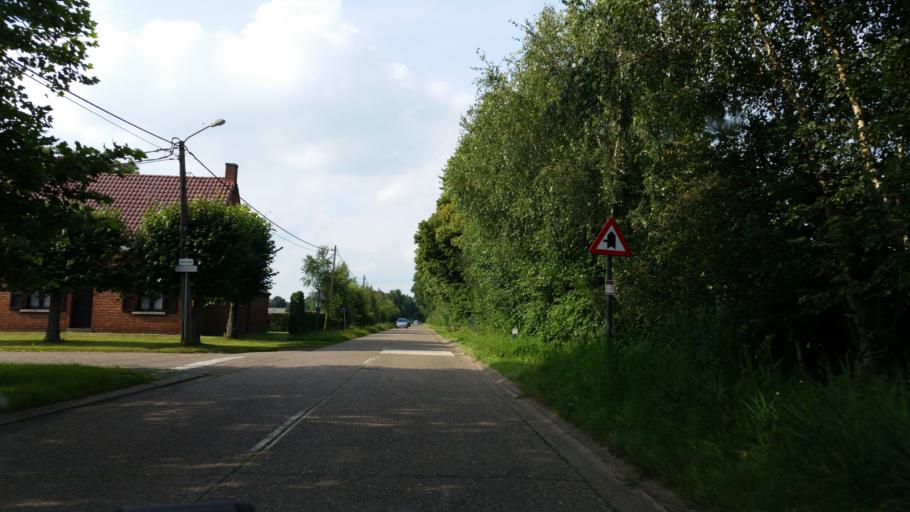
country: BE
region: Flanders
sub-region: Provincie Antwerpen
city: Kasterlee
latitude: 51.2362
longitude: 4.9200
